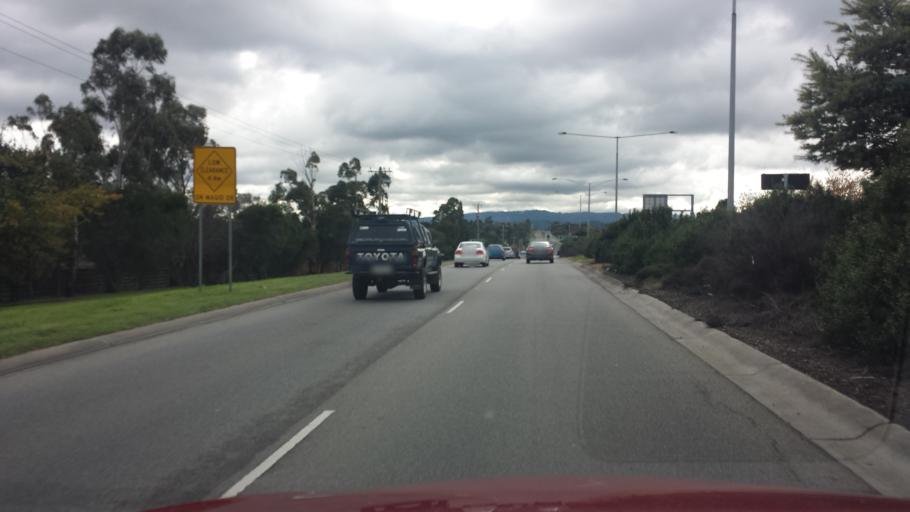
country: AU
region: Victoria
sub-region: Casey
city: Narre Warren
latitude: -38.0160
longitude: 145.3088
